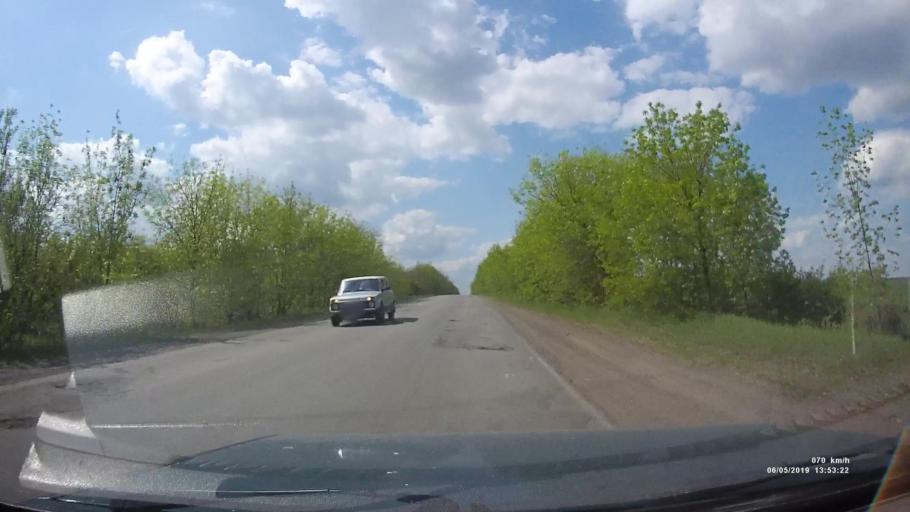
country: RU
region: Rostov
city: Melikhovskaya
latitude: 47.6678
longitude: 40.4634
